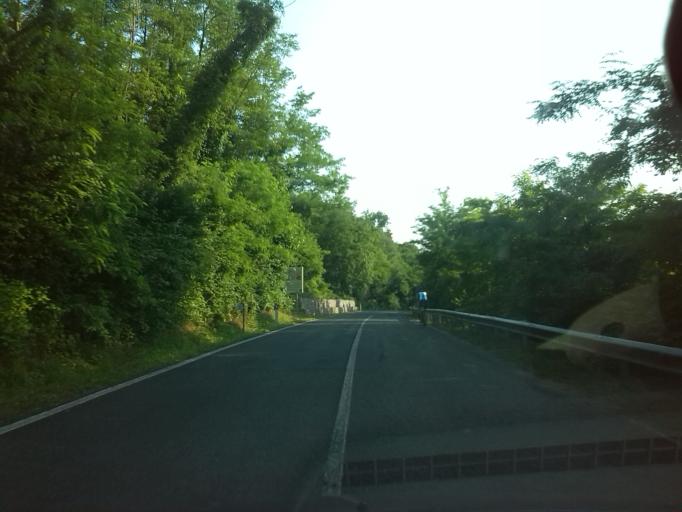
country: IT
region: Friuli Venezia Giulia
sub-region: Provincia di Gorizia
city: Dolegna del Collio
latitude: 46.0123
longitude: 13.4719
